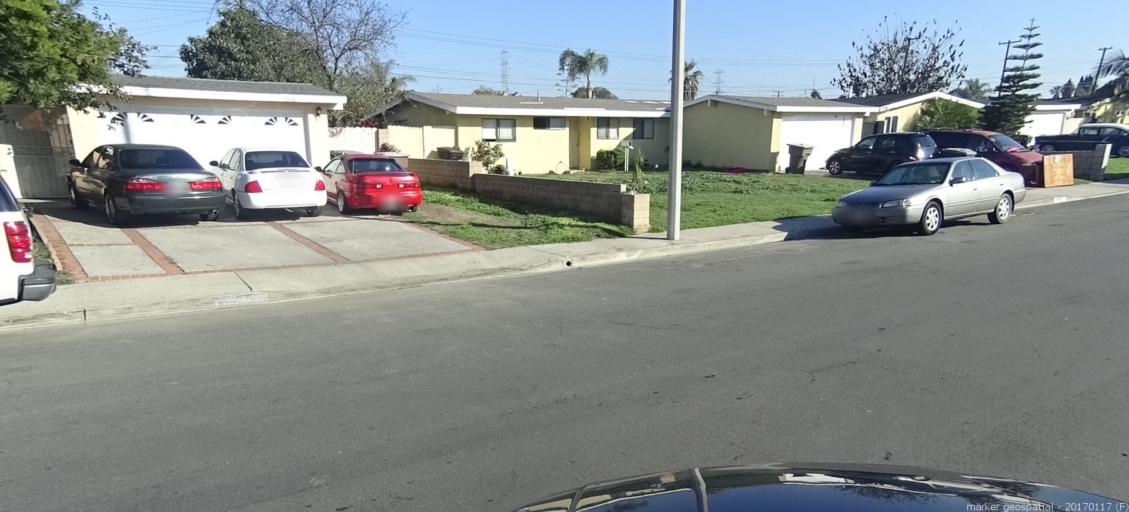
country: US
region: California
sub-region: Orange County
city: Stanton
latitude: 33.8039
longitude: -117.9648
